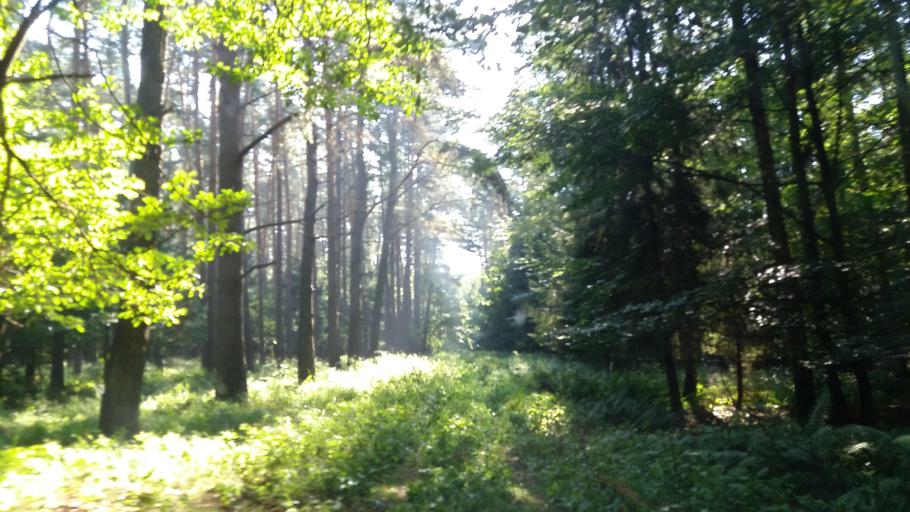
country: PL
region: West Pomeranian Voivodeship
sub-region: Powiat choszczenski
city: Pelczyce
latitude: 52.9741
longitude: 15.3476
